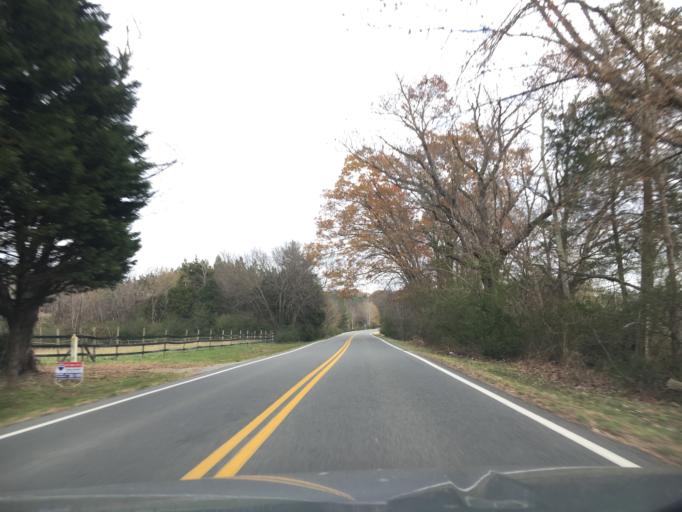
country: US
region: Virginia
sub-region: Cumberland County
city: Cumberland
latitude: 37.4558
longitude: -78.3090
